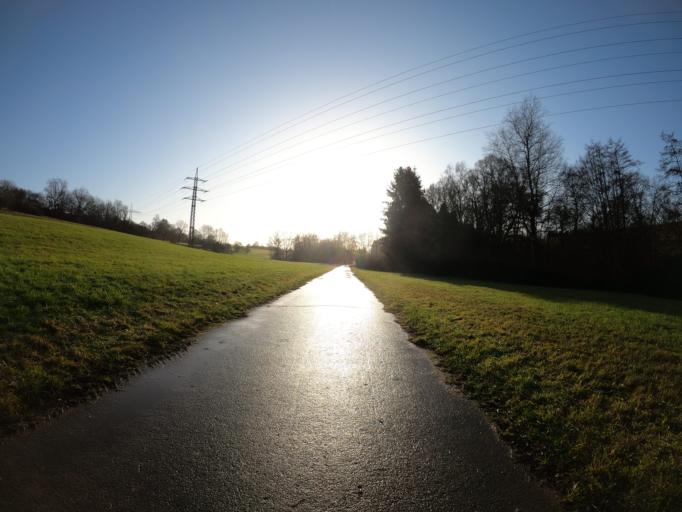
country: DE
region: Baden-Wuerttemberg
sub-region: Regierungsbezirk Stuttgart
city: Uhingen
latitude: 48.6972
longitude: 9.6171
